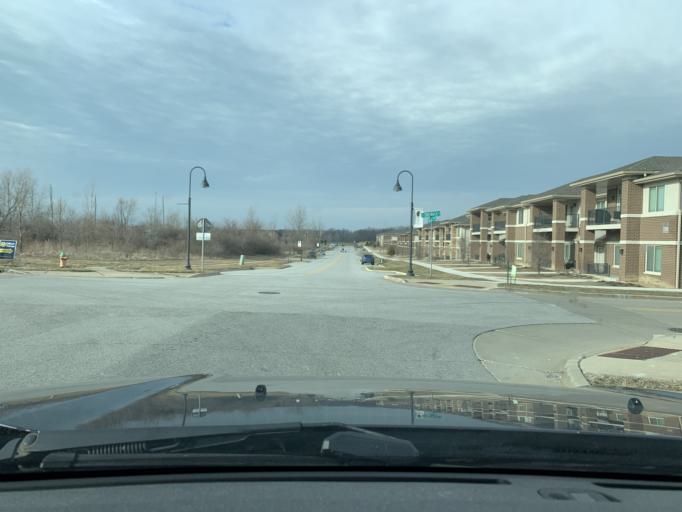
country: US
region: Indiana
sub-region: Porter County
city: Chesterton
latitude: 41.5862
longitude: -87.0412
